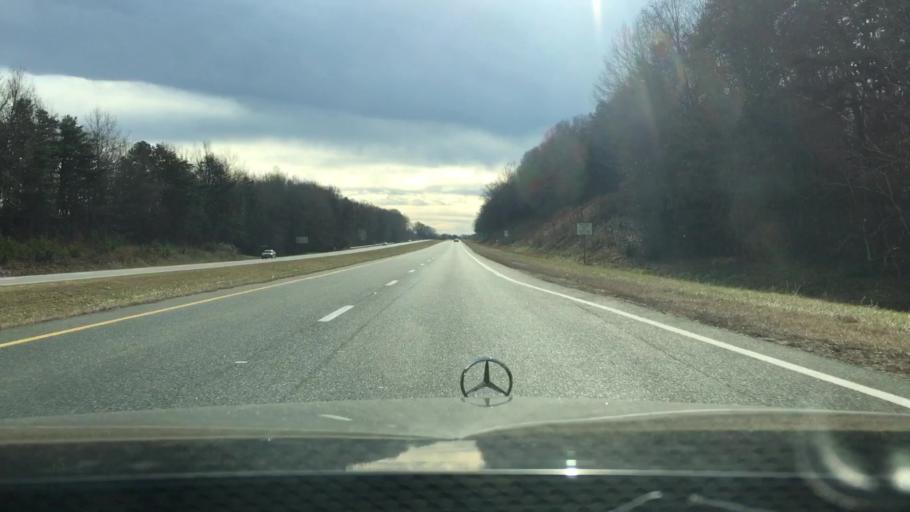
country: US
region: Virginia
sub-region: Pittsylvania County
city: Motley
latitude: 37.0754
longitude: -79.3370
